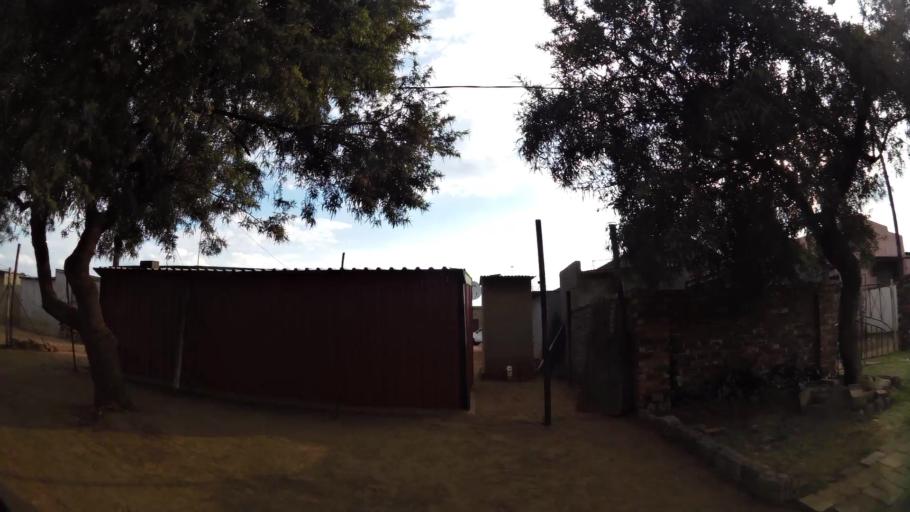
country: ZA
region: Gauteng
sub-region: Sedibeng District Municipality
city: Vanderbijlpark
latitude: -26.6777
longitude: 27.8689
